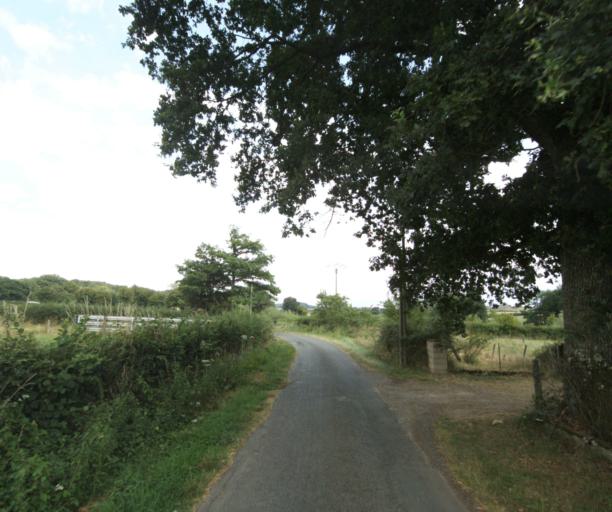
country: FR
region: Bourgogne
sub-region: Departement de Saone-et-Loire
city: Gueugnon
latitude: 46.6111
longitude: 4.0822
